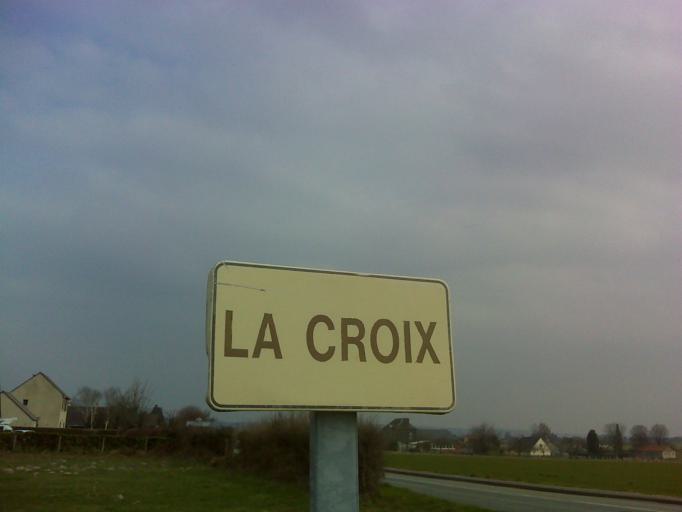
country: FR
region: Haute-Normandie
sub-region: Departement de la Seine-Maritime
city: Caudebec-en-Caux
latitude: 49.5079
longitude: 0.7214
